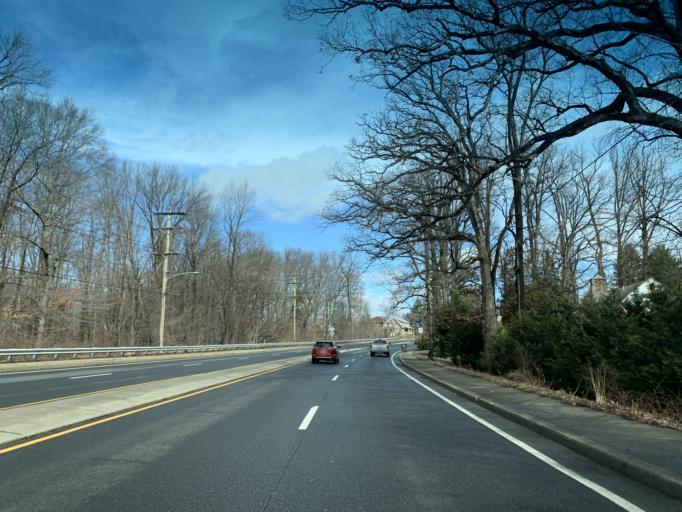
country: US
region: Delaware
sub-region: New Castle County
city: Newark
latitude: 39.6879
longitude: -75.7350
